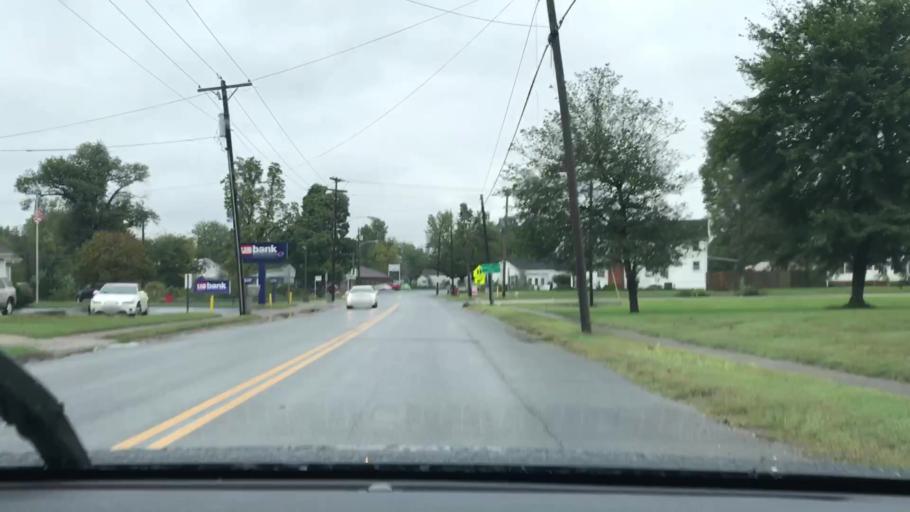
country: US
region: Kentucky
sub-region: McLean County
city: Calhoun
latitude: 37.5431
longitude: -87.2594
